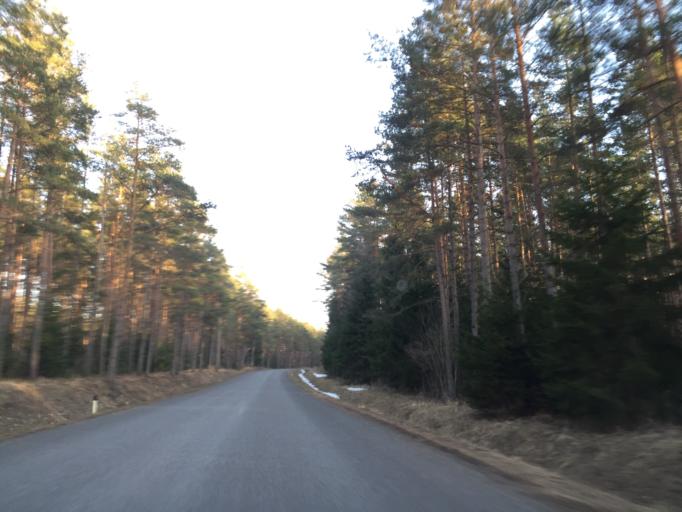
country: EE
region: Laeaene
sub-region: Lihula vald
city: Lihula
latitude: 58.4693
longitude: 23.7164
